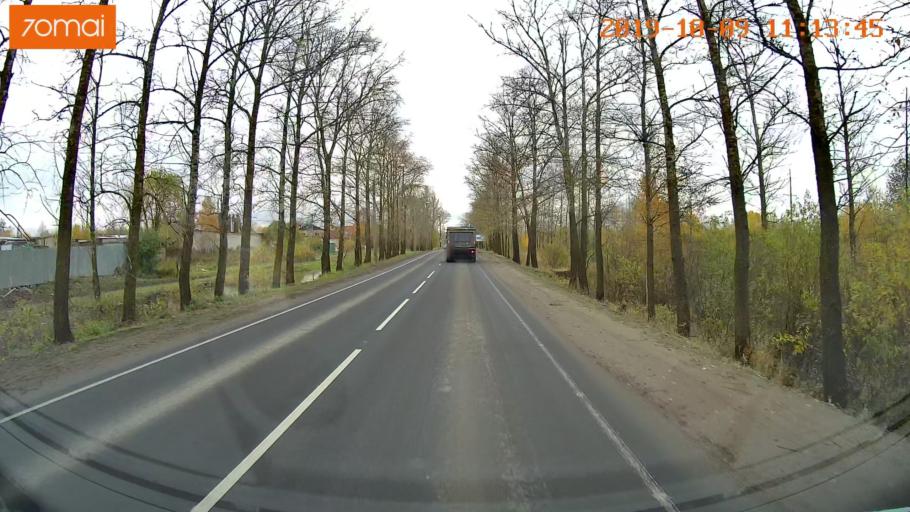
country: RU
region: Vologda
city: Vologda
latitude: 59.1840
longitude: 39.8466
